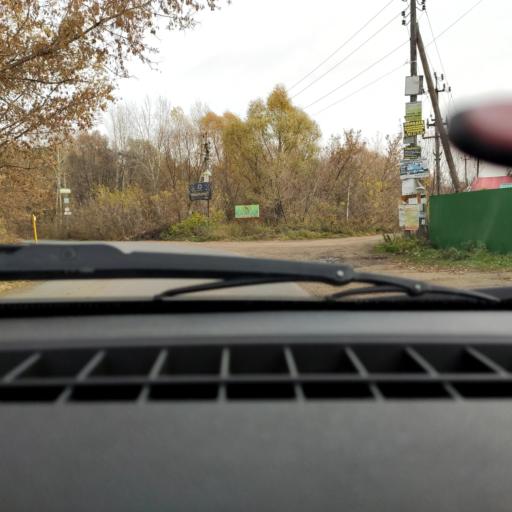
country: RU
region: Bashkortostan
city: Iglino
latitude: 54.8129
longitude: 56.1924
